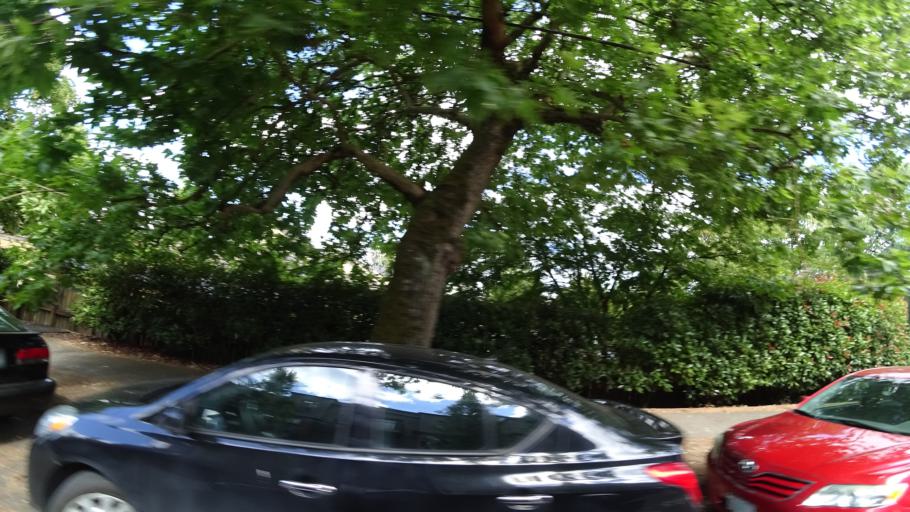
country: US
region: Oregon
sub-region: Multnomah County
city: Portland
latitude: 45.5270
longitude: -122.7005
